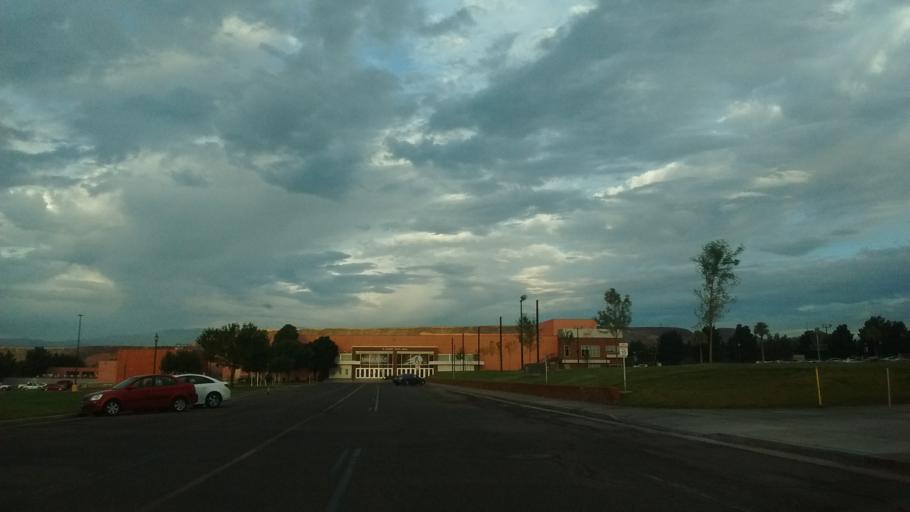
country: US
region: Utah
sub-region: Washington County
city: Saint George
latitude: 37.1014
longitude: -113.5647
